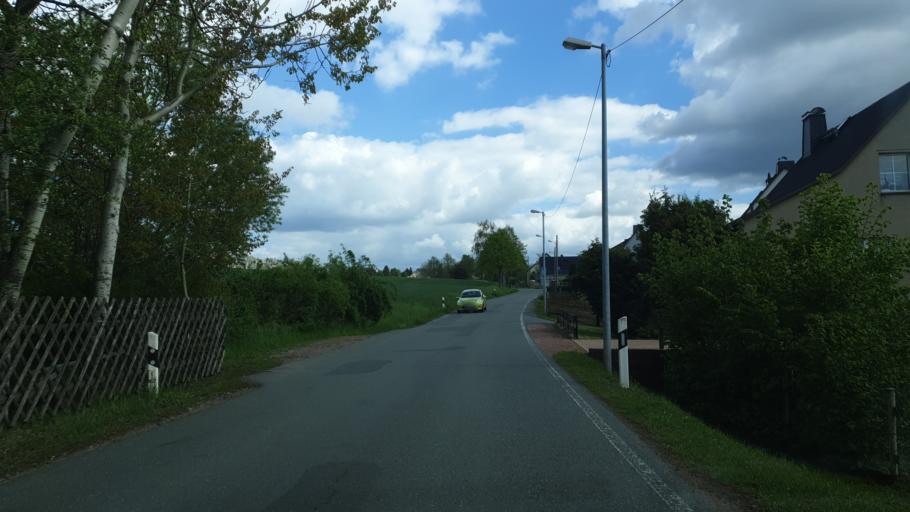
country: DE
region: Saxony
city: Kirchberg
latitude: 50.7780
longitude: 12.7821
